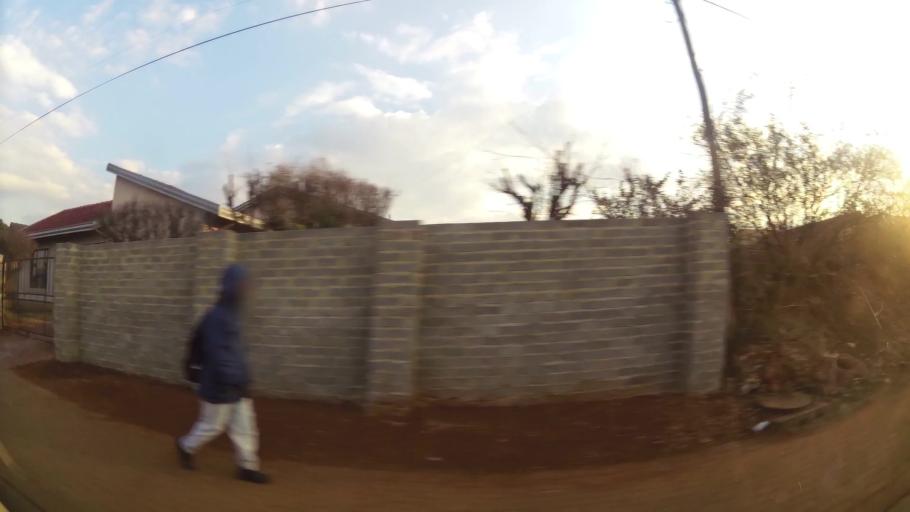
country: ZA
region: Gauteng
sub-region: City of Johannesburg Metropolitan Municipality
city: Orange Farm
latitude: -26.5619
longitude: 27.8606
